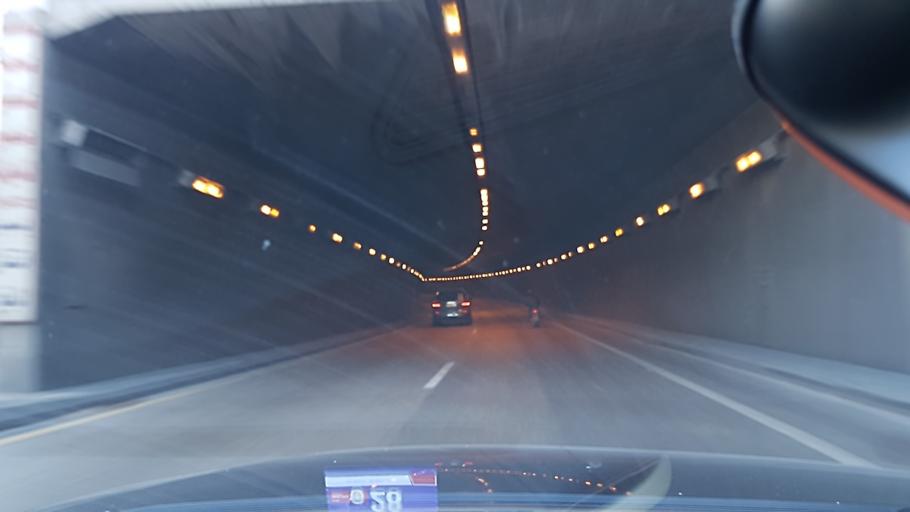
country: LB
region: Mont-Liban
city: Baabda
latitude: 33.8318
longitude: 35.5007
